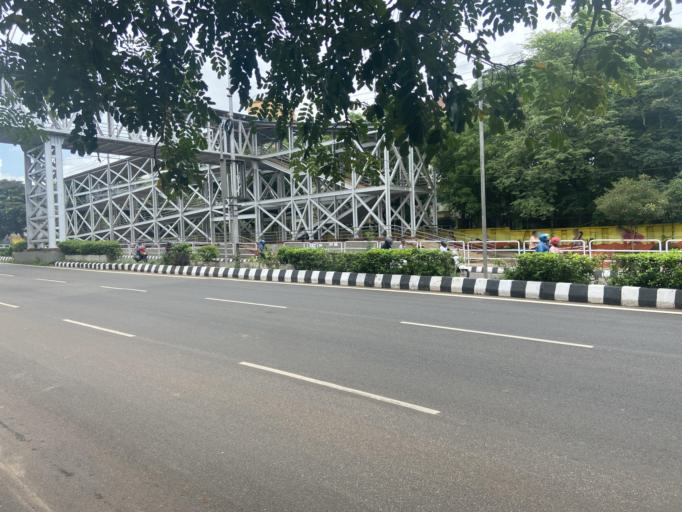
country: IN
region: Odisha
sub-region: Khordha
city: Bhubaneshwar
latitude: 20.2893
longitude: 85.8261
